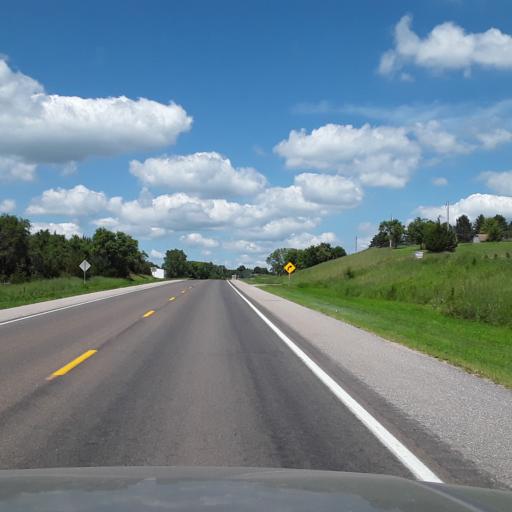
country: US
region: Nebraska
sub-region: Nance County
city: Genoa
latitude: 41.4553
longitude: -97.7252
